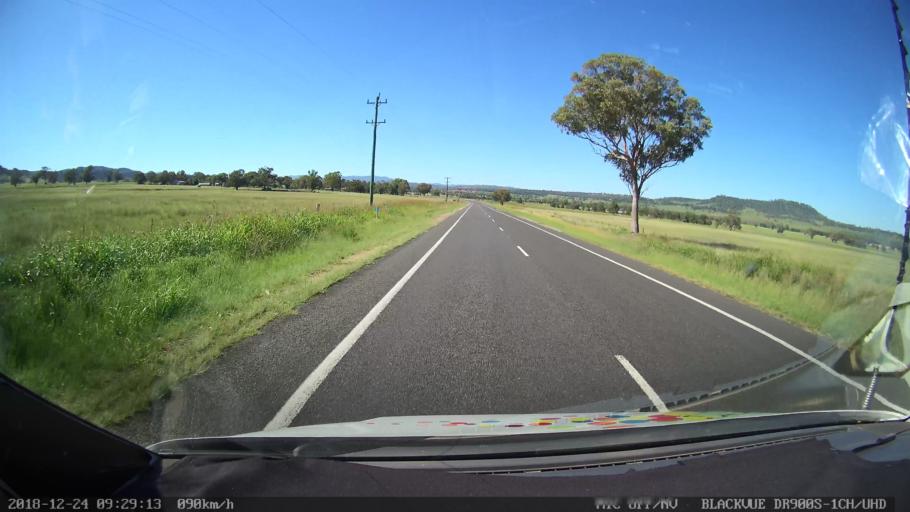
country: AU
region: New South Wales
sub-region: Liverpool Plains
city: Quirindi
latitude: -31.5476
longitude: 150.6924
